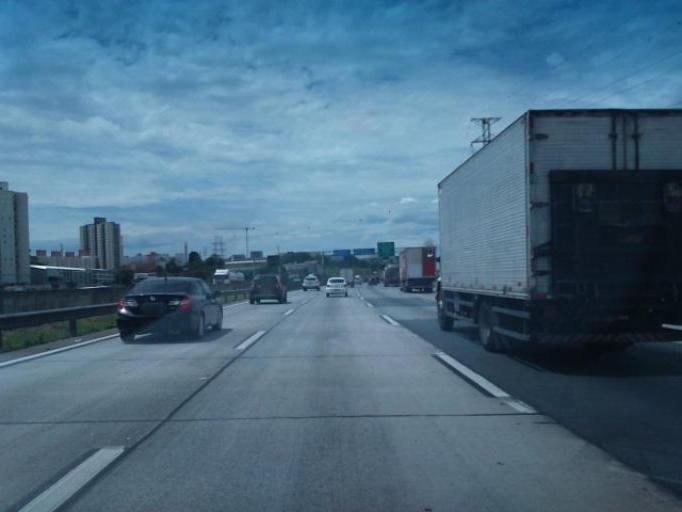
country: BR
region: Sao Paulo
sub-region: Carapicuiba
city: Carapicuiba
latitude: -23.5373
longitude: -46.8179
